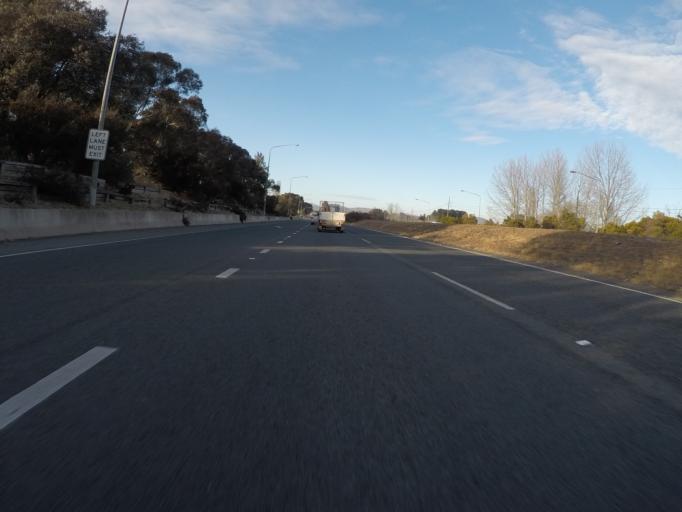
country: AU
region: Australian Capital Territory
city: Forrest
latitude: -35.3351
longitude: 149.1622
